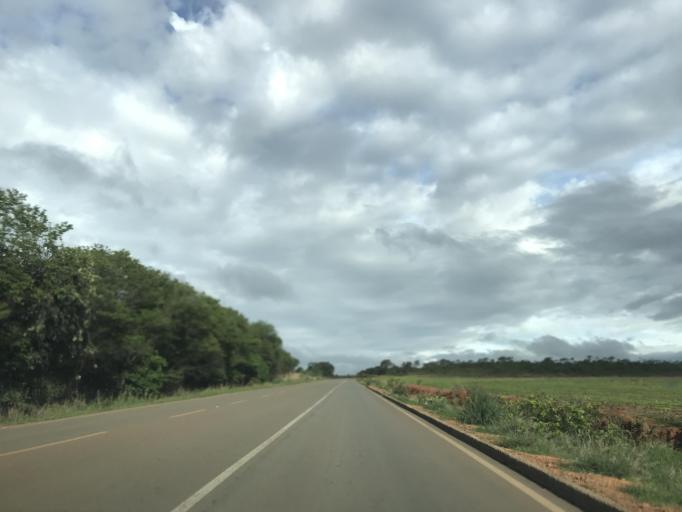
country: BR
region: Goias
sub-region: Vianopolis
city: Vianopolis
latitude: -16.5767
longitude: -48.3016
